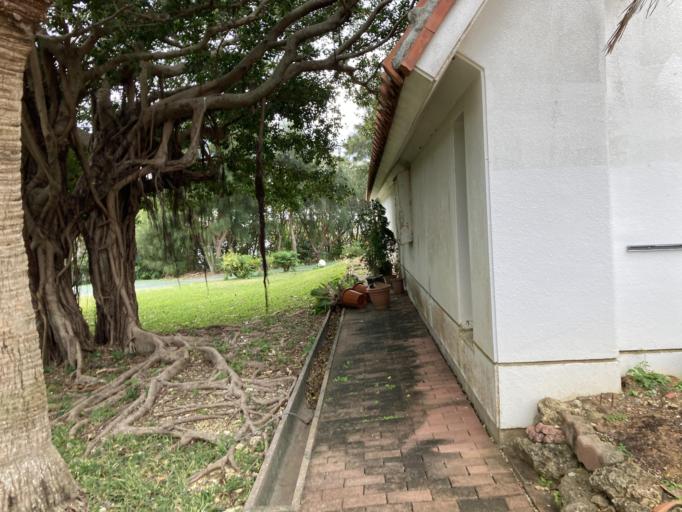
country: JP
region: Okinawa
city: Ishikawa
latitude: 26.4340
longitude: 127.7186
